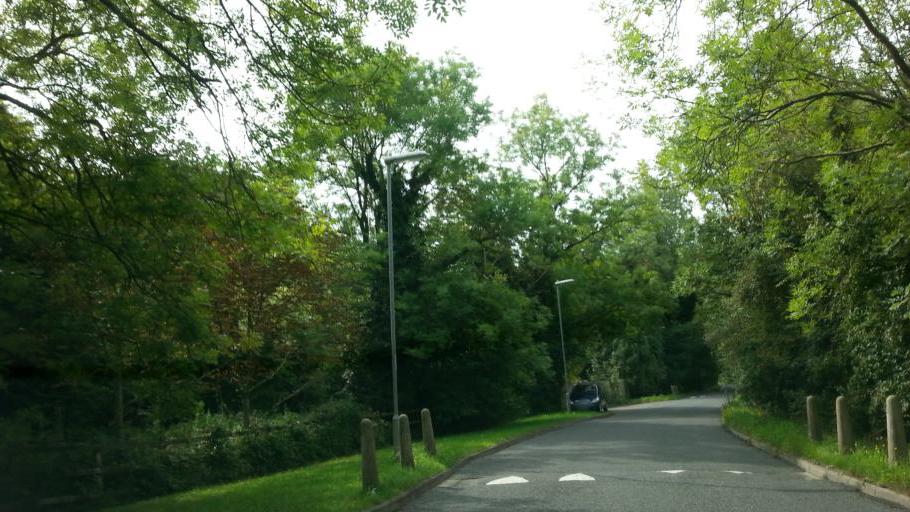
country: GB
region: England
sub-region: Cambridgeshire
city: Comberton
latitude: 52.2053
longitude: -0.0252
